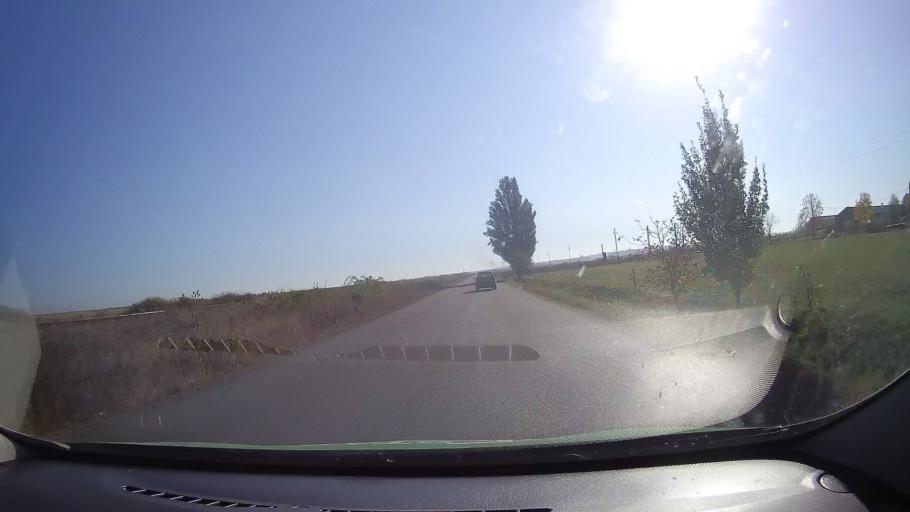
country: RO
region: Satu Mare
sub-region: Comuna Santau
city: Santau
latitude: 47.5061
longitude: 22.5298
